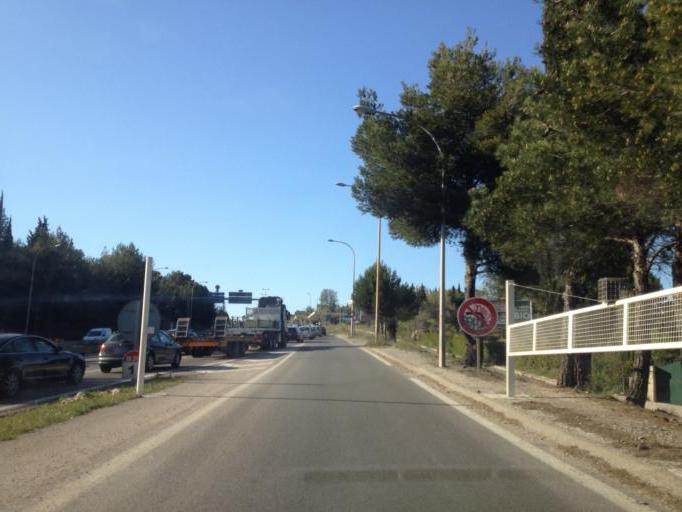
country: FR
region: Provence-Alpes-Cote d'Azur
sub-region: Departement des Bouches-du-Rhone
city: Aix-en-Provence
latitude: 43.5404
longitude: 5.4329
